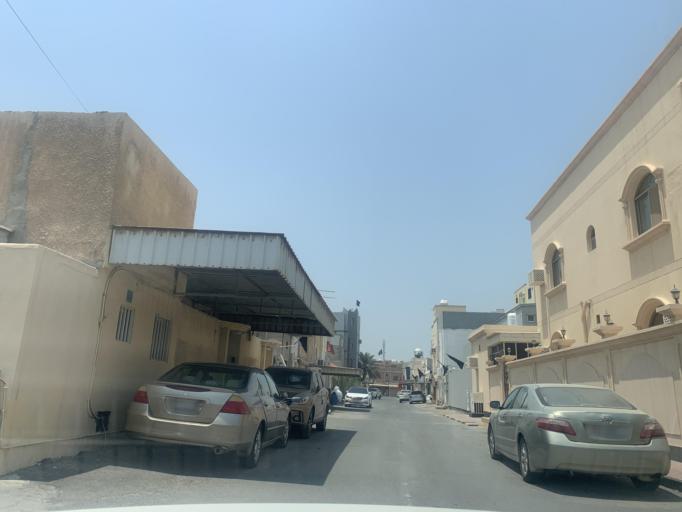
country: BH
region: Central Governorate
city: Madinat Hamad
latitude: 26.1429
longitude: 50.4626
